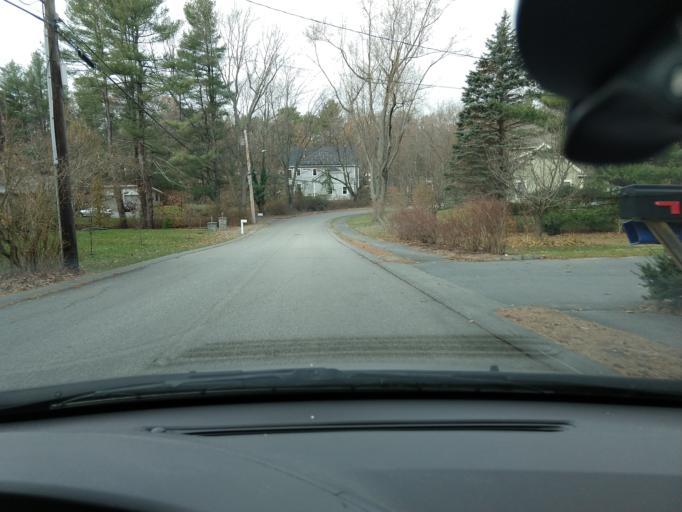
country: US
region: Massachusetts
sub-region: Middlesex County
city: Bedford
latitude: 42.4951
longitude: -71.2483
